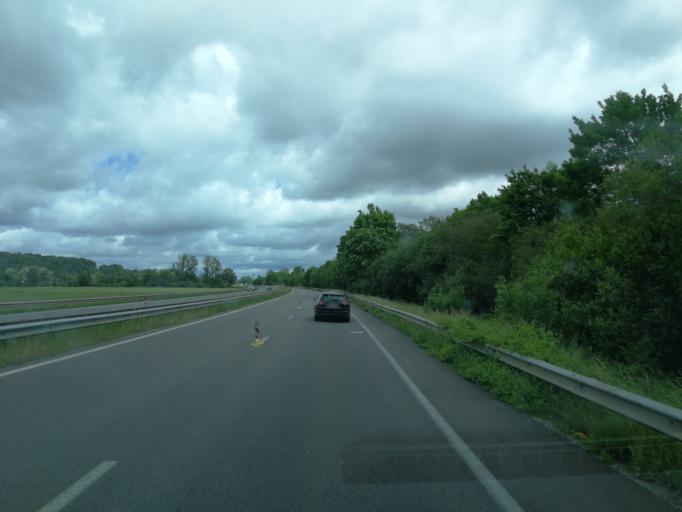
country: FR
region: Haute-Normandie
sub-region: Departement de l'Eure
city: Heudreville-sur-Eure
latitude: 49.1517
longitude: 1.1827
